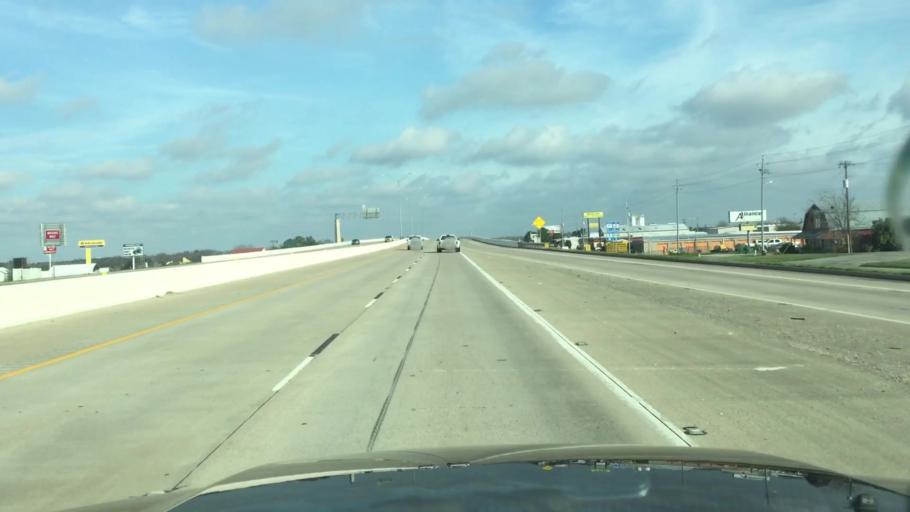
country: US
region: Texas
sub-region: Washington County
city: Brenham
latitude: 30.1427
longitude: -96.3729
